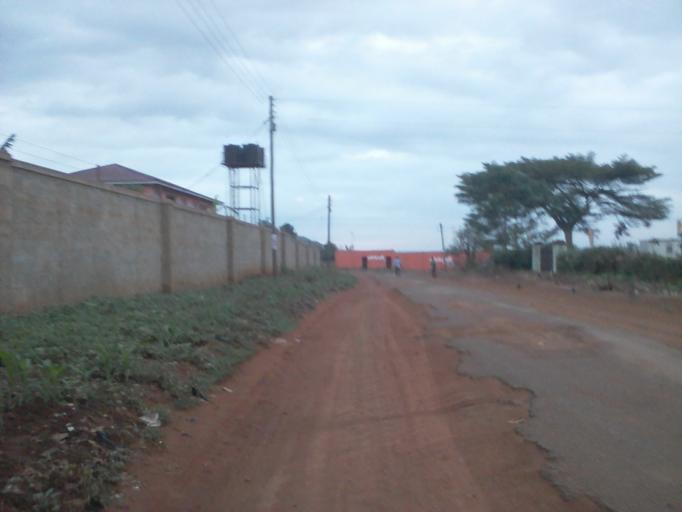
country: UG
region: Eastern Region
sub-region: Mbale District
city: Mbale
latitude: 1.0736
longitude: 34.1791
